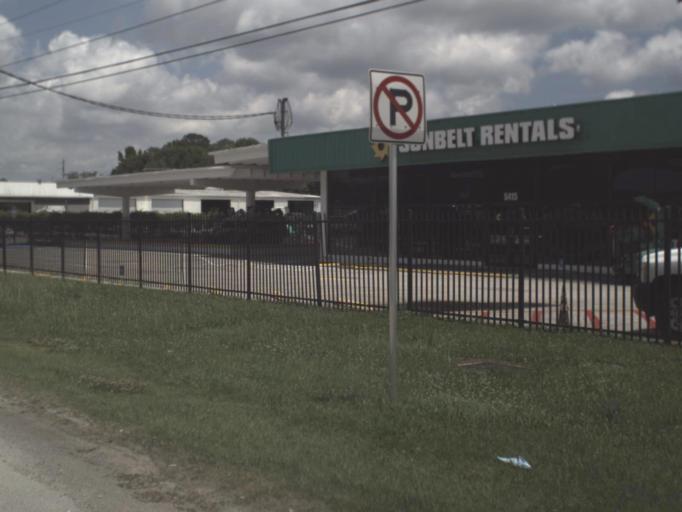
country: US
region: Florida
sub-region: Duval County
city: Jacksonville
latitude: 30.2680
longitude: -81.6195
